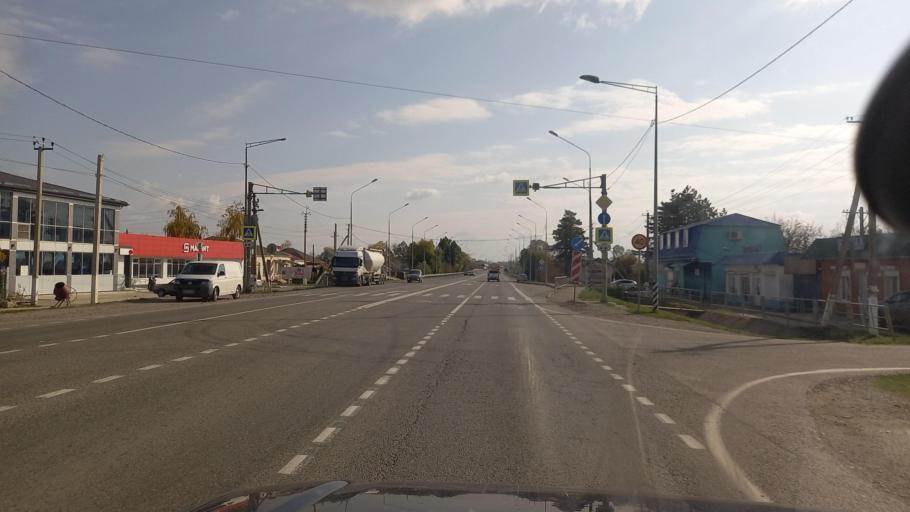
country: RU
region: Krasnodarskiy
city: Novoukrainskiy
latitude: 44.8958
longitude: 38.0533
